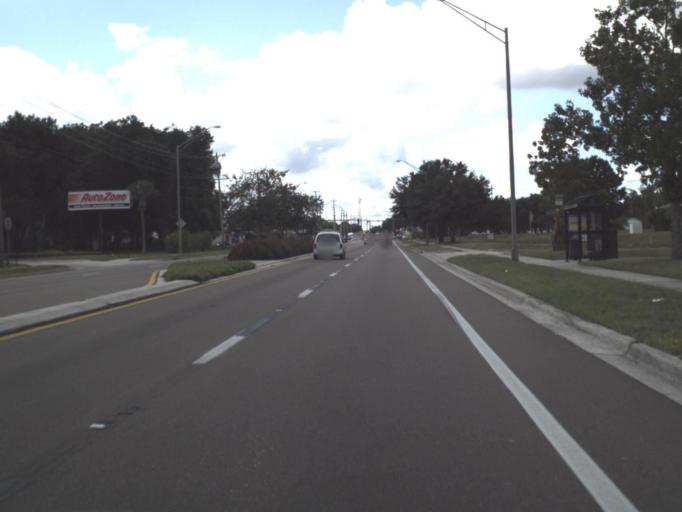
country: US
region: Florida
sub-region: Polk County
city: Lakeland
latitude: 28.0658
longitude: -81.9574
